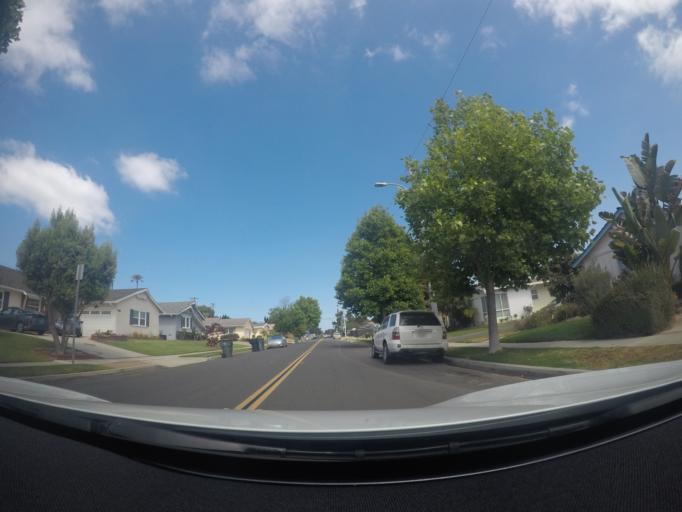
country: US
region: California
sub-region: Los Angeles County
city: Rolling Hills Estates
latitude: 33.8077
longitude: -118.3687
